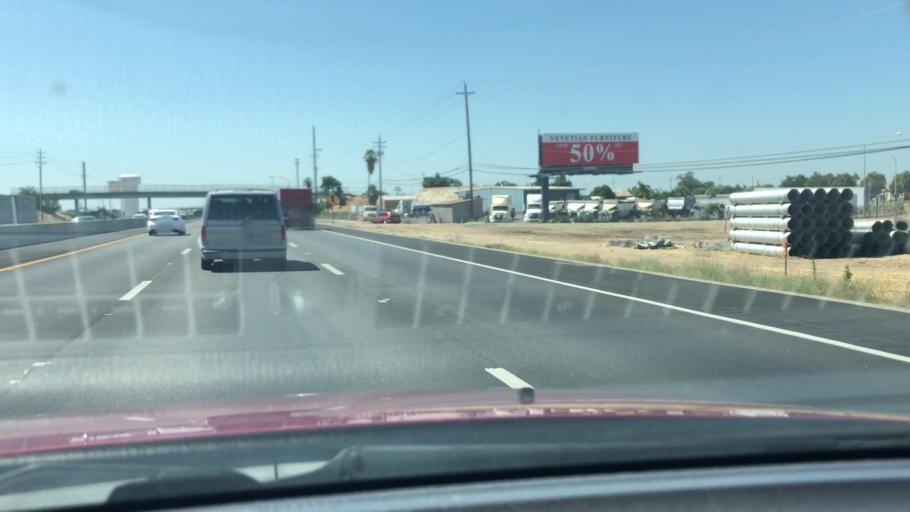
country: US
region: California
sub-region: San Joaquin County
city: Ripon
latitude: 37.7451
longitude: -121.1297
